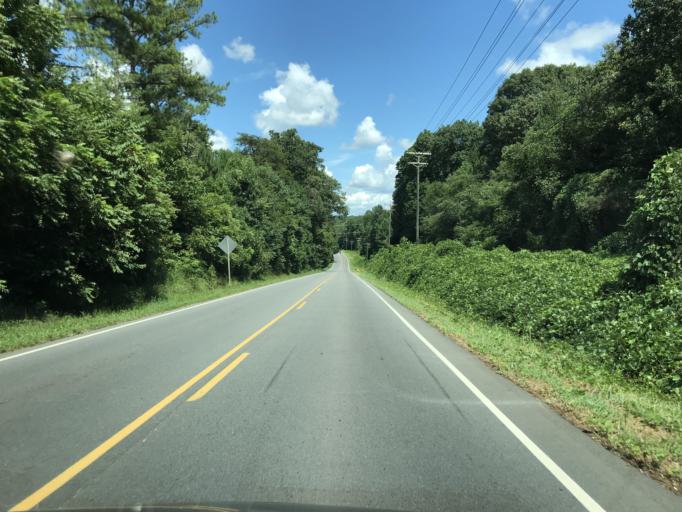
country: US
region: North Carolina
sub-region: Lincoln County
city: Pumpkin Center
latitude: 35.5057
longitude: -81.1696
